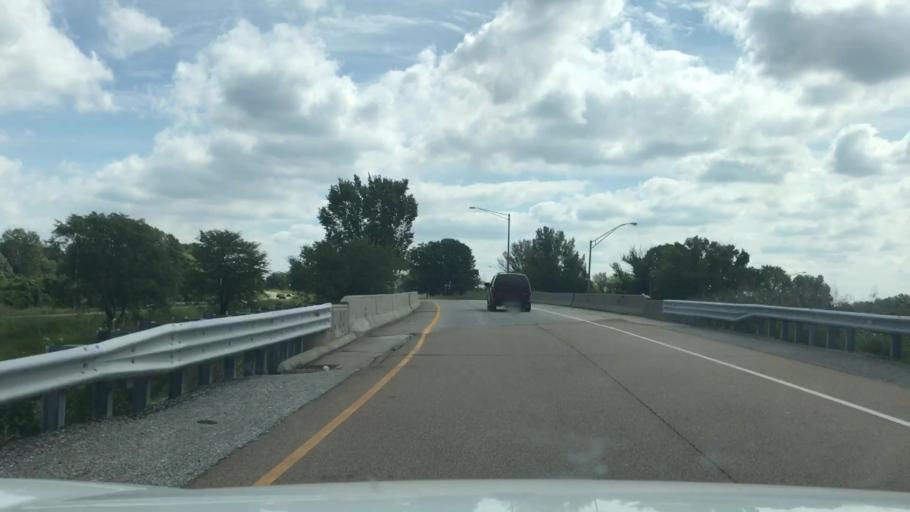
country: US
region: Illinois
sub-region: Saint Clair County
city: Alorton
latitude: 38.5484
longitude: -90.0673
